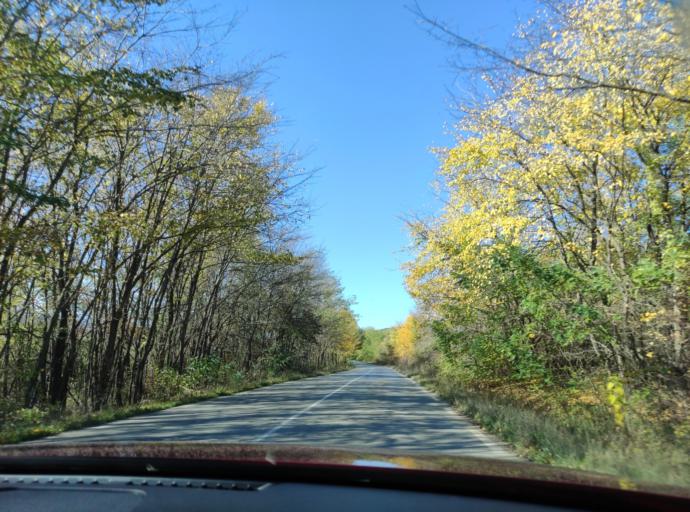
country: BG
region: Montana
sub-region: Obshtina Chiprovtsi
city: Chiprovtsi
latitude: 43.4241
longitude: 23.0130
